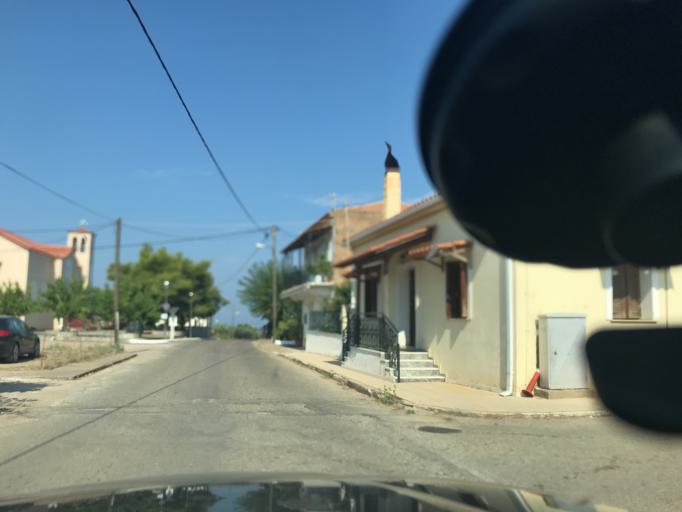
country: GR
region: West Greece
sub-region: Nomos Ileias
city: Kardamas
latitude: 37.7175
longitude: 21.3318
